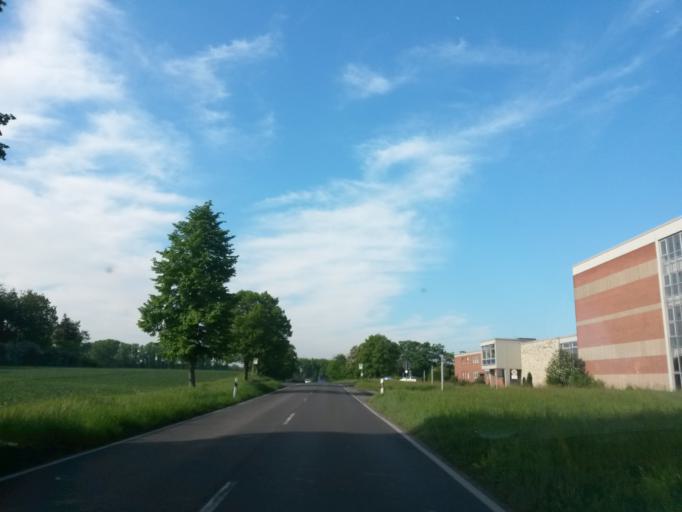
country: DE
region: North Rhine-Westphalia
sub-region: Regierungsbezirk Koln
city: Troisdorf
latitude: 50.7733
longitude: 7.1338
